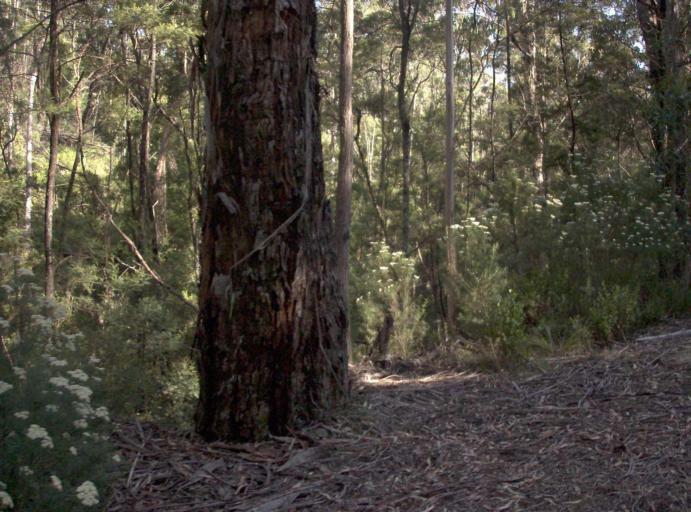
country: AU
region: Victoria
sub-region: East Gippsland
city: Lakes Entrance
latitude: -37.6387
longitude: 148.4807
